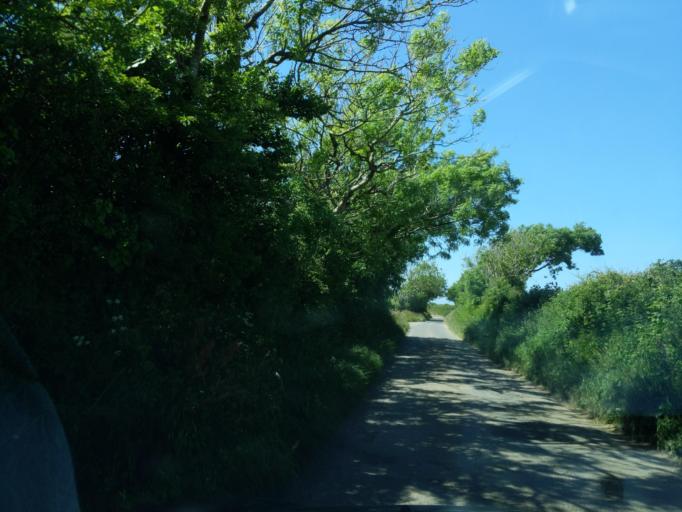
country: GB
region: England
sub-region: Cornwall
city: Wadebridge
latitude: 50.5781
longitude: -4.8314
